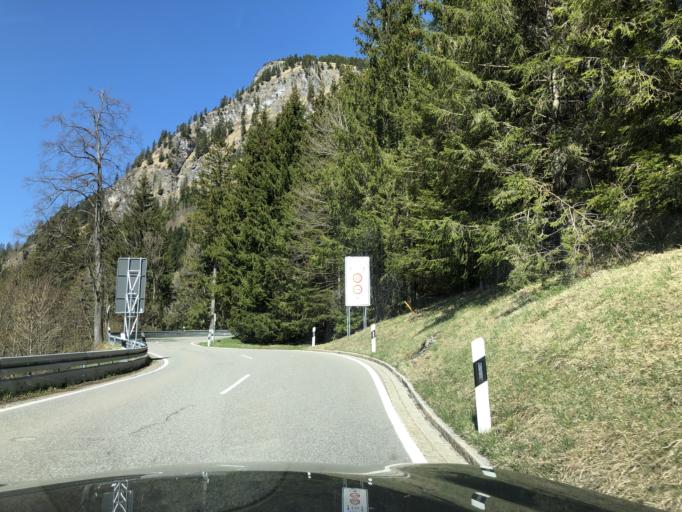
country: AT
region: Tyrol
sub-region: Politischer Bezirk Reutte
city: Schattwald
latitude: 47.5118
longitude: 10.3846
